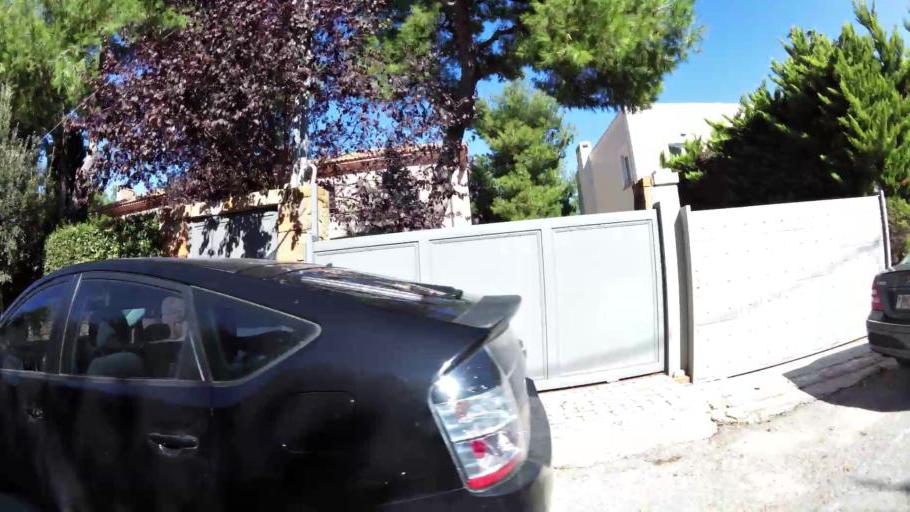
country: GR
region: Attica
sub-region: Nomarchia Anatolikis Attikis
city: Dionysos
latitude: 38.1056
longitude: 23.8814
